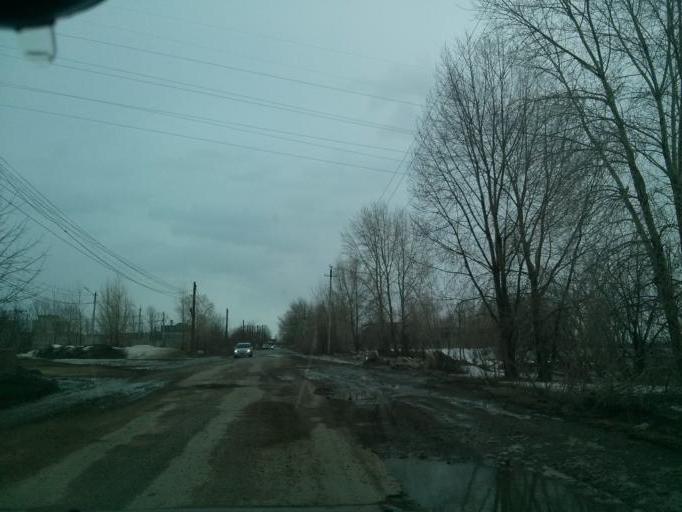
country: RU
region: Nizjnij Novgorod
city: Afonino
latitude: 56.2922
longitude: 44.1120
